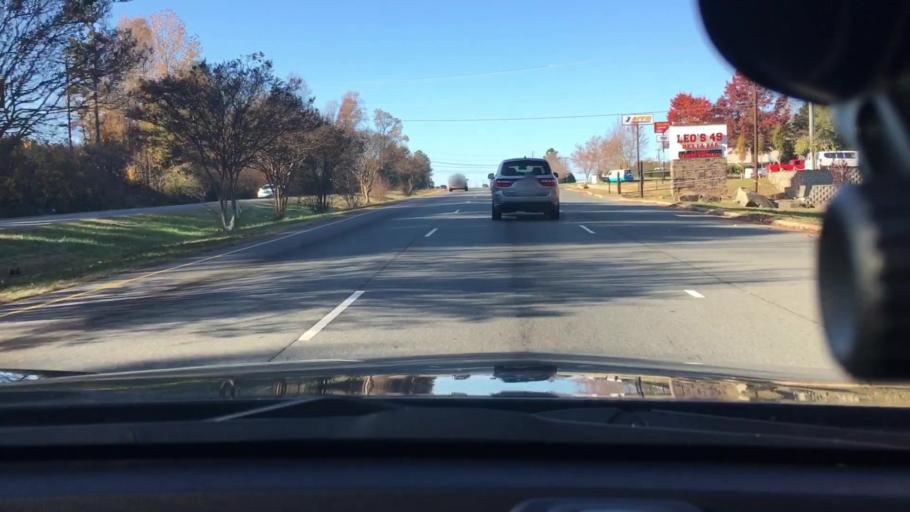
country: US
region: North Carolina
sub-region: Cabarrus County
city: Harrisburg
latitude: 35.2924
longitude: -80.7516
